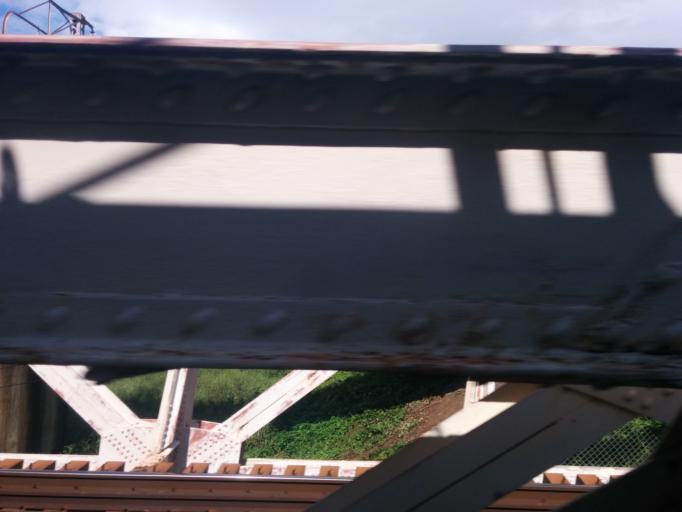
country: JP
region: Kyoto
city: Muko
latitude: 34.9757
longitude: 135.7214
